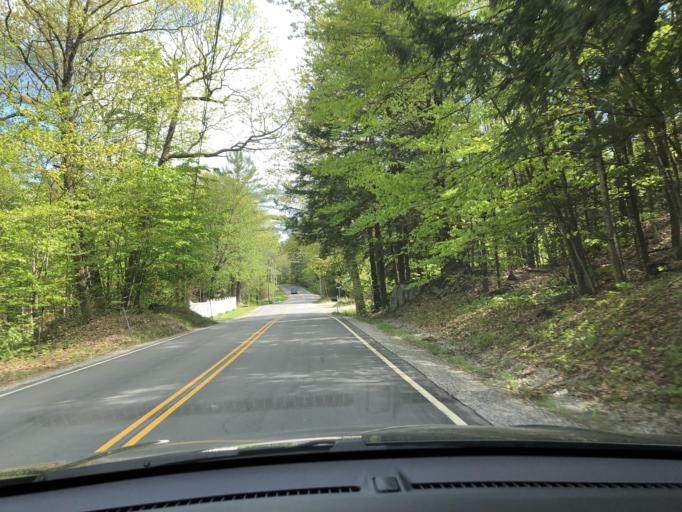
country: US
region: New Hampshire
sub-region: Merrimack County
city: New London
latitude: 43.4162
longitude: -72.0358
